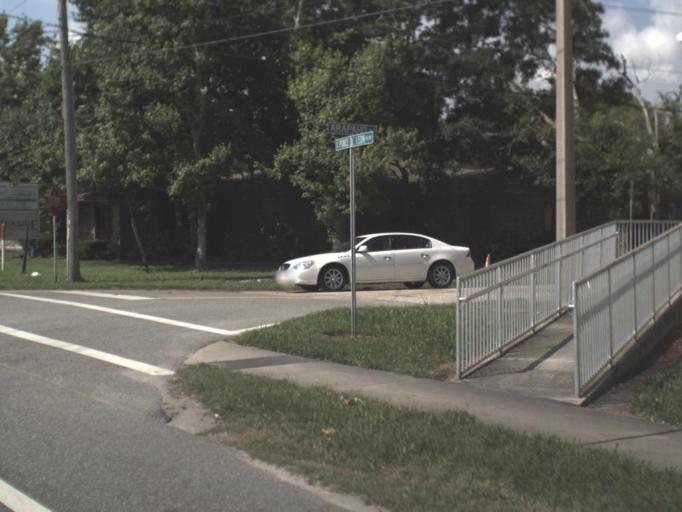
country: US
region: Florida
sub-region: Saint Johns County
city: Saint Augustine
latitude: 29.8790
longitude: -81.3249
